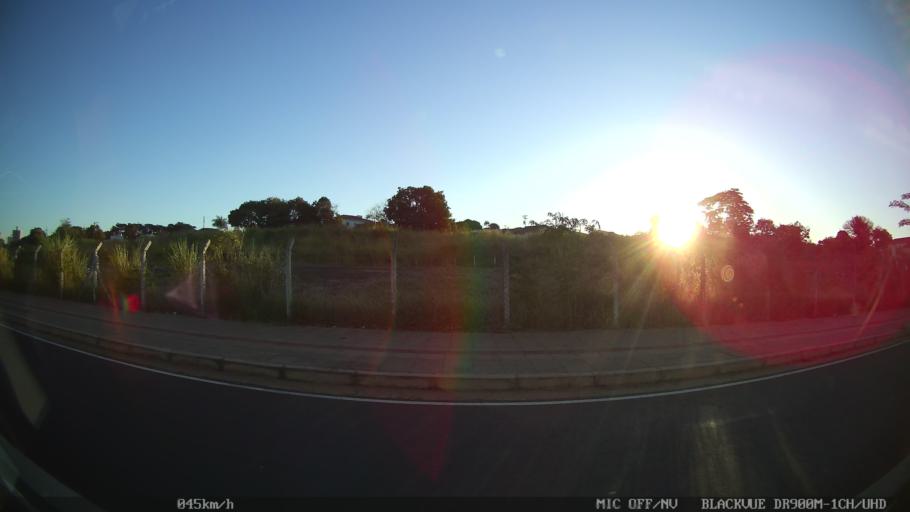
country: BR
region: Sao Paulo
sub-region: Sao Jose Do Rio Preto
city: Sao Jose do Rio Preto
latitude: -20.7939
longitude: -49.3770
